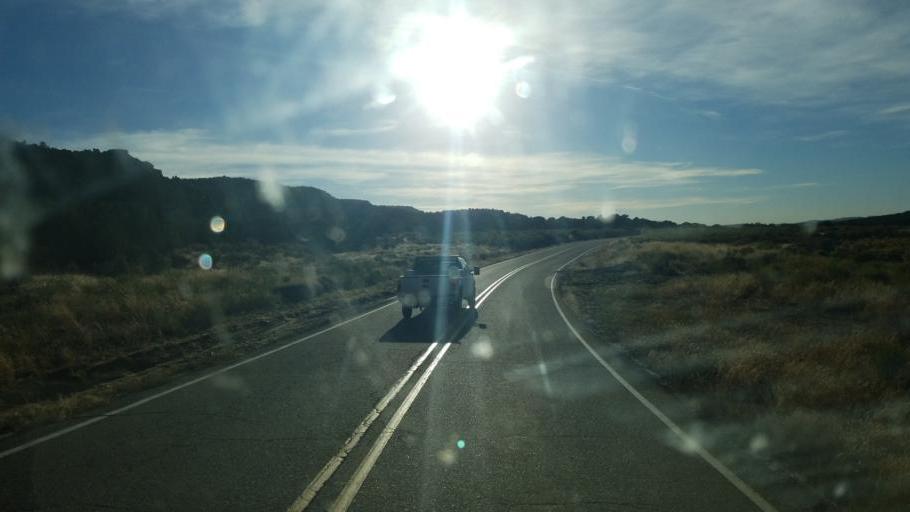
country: US
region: New Mexico
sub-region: San Juan County
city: Bloomfield
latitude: 36.7370
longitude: -107.7371
